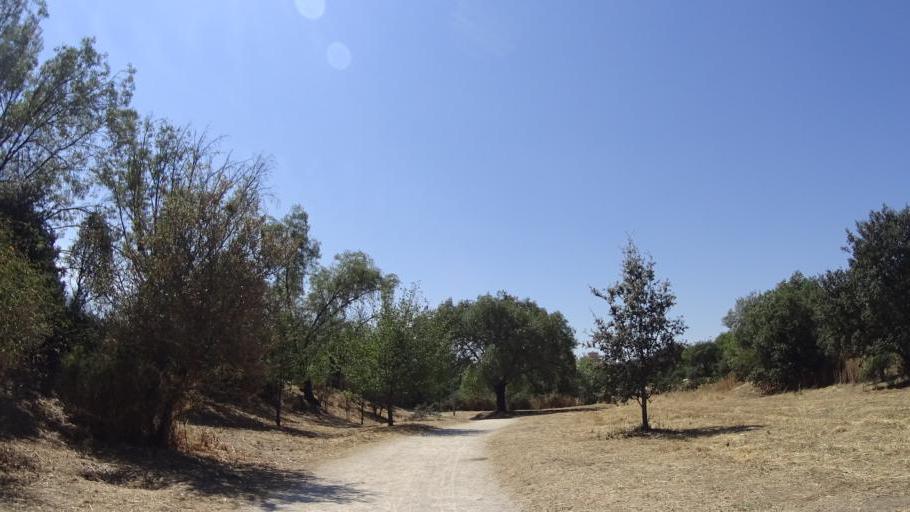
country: ES
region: Madrid
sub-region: Provincia de Madrid
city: Boadilla del Monte
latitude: 40.4094
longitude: -3.8698
